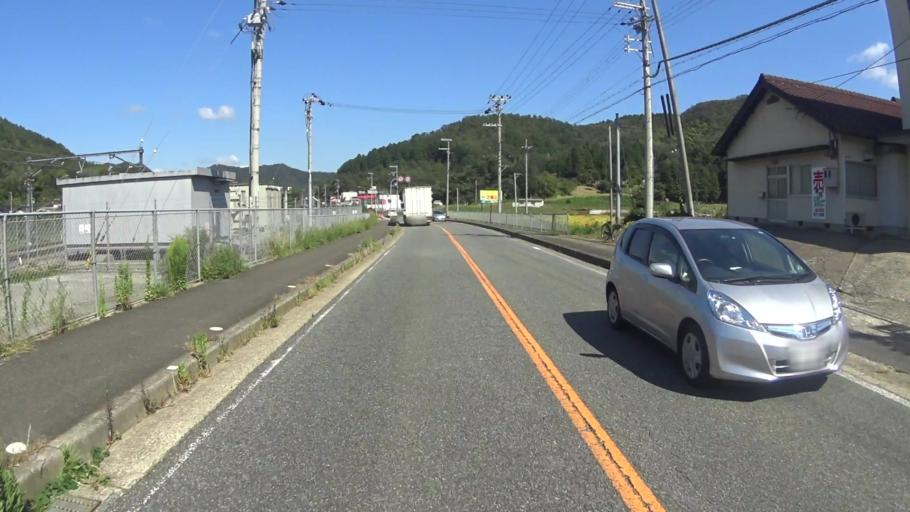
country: JP
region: Kyoto
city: Ayabe
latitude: 35.3469
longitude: 135.3120
